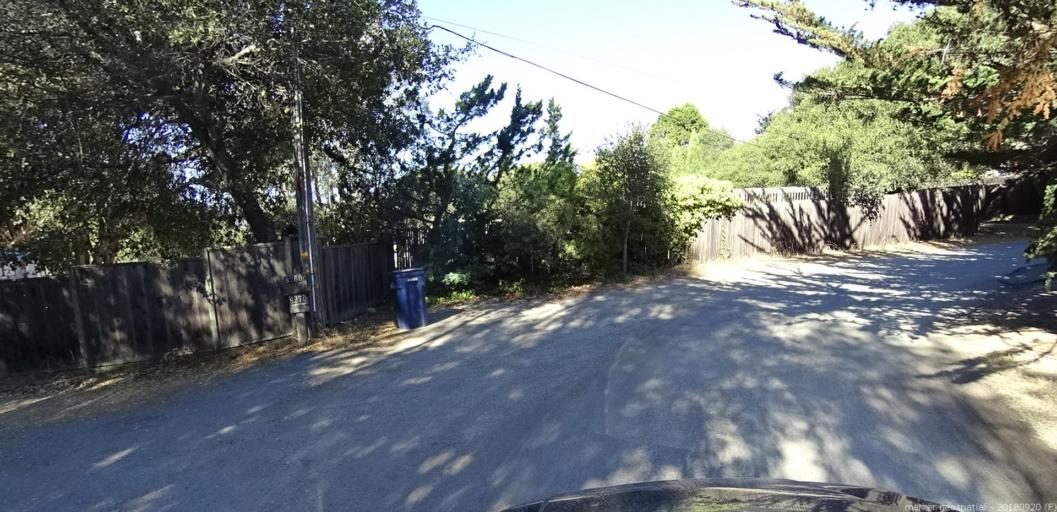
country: US
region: California
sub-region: Monterey County
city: Del Rey Oaks
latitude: 36.5316
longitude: -121.8313
